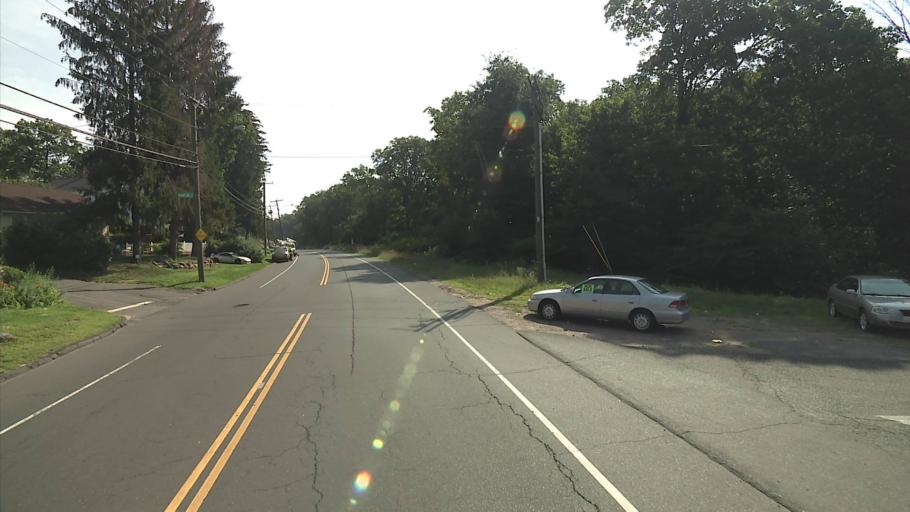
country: US
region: Connecticut
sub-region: New Haven County
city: Wolcott
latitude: 41.5532
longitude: -72.9979
